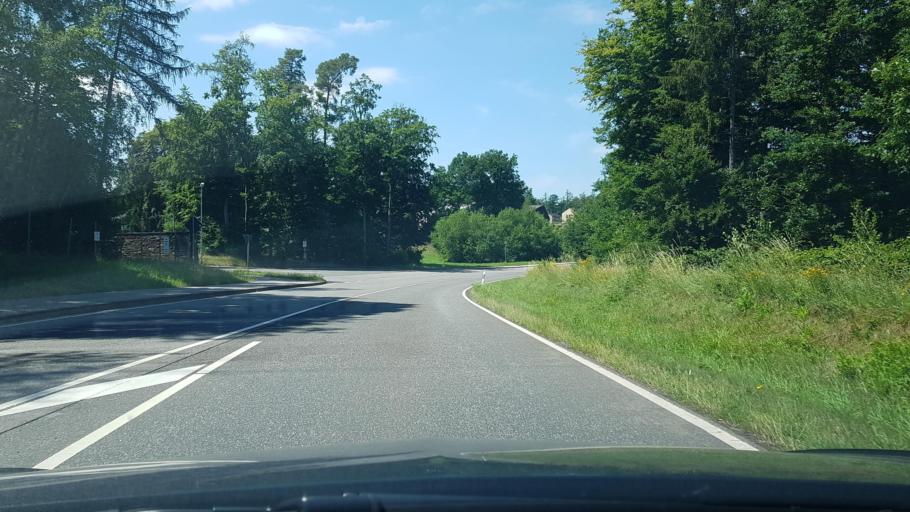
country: DE
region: Rheinland-Pfalz
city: Ediger-Eller
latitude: 50.1343
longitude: 7.1382
